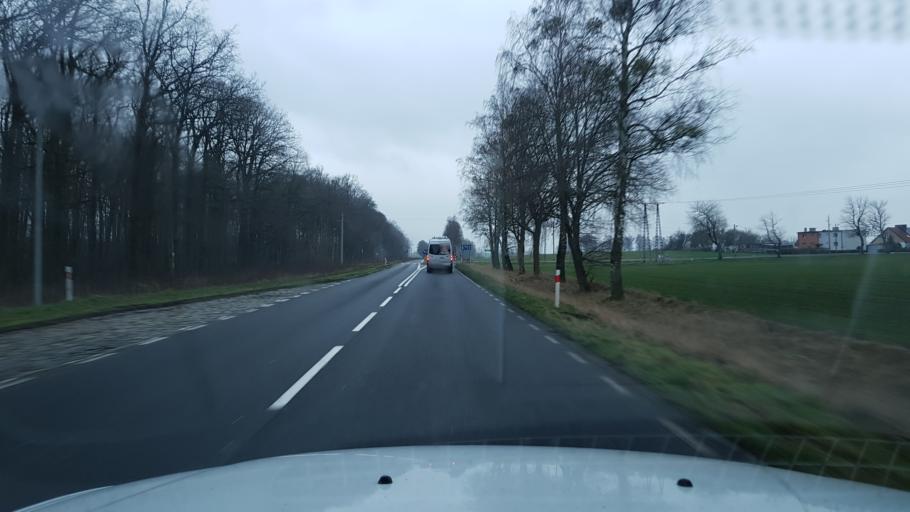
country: PL
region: West Pomeranian Voivodeship
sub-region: Powiat gryficki
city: Gryfice
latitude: 53.8872
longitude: 15.2092
